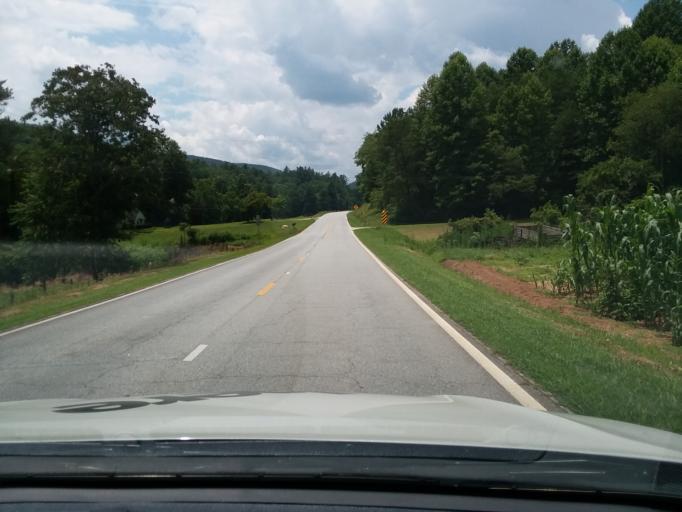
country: US
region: Georgia
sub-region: Rabun County
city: Mountain City
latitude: 34.8873
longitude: -83.3246
